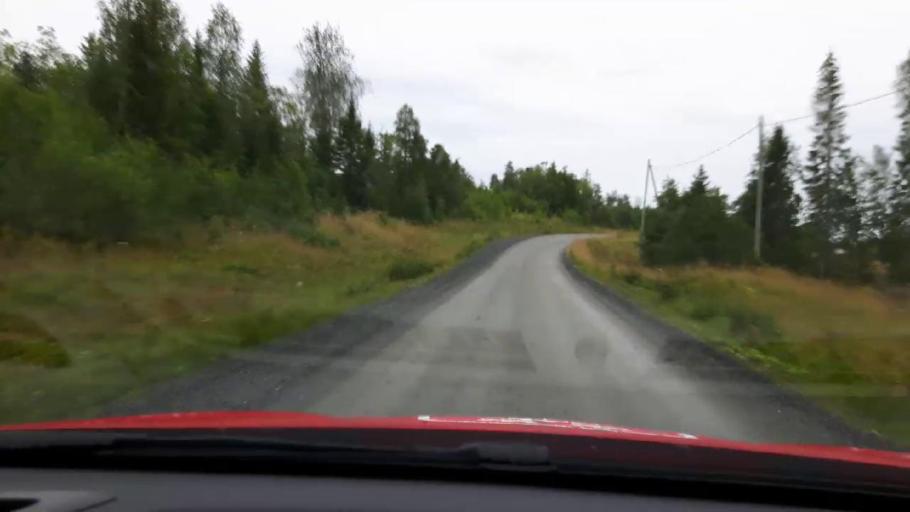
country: SE
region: Jaemtland
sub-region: Are Kommun
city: Are
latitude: 63.4945
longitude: 12.7659
